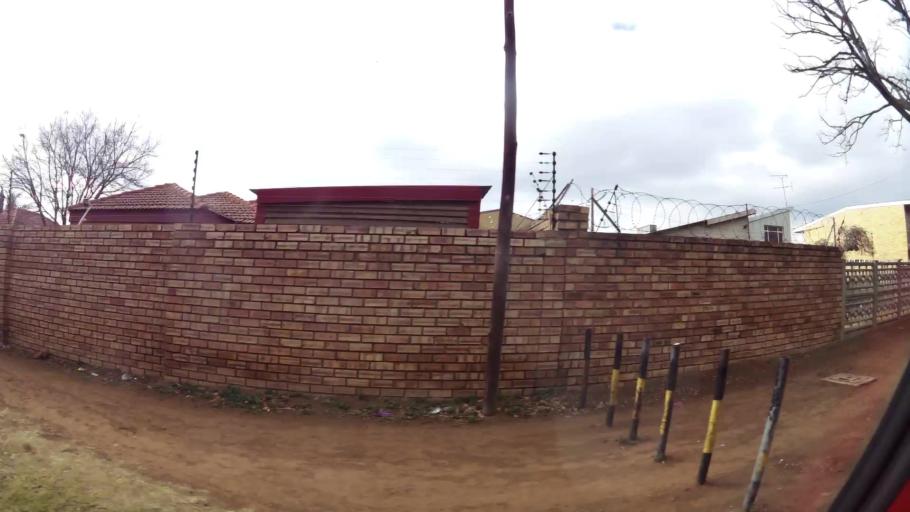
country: ZA
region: Gauteng
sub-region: Sedibeng District Municipality
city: Vanderbijlpark
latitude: -26.6922
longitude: 27.8389
